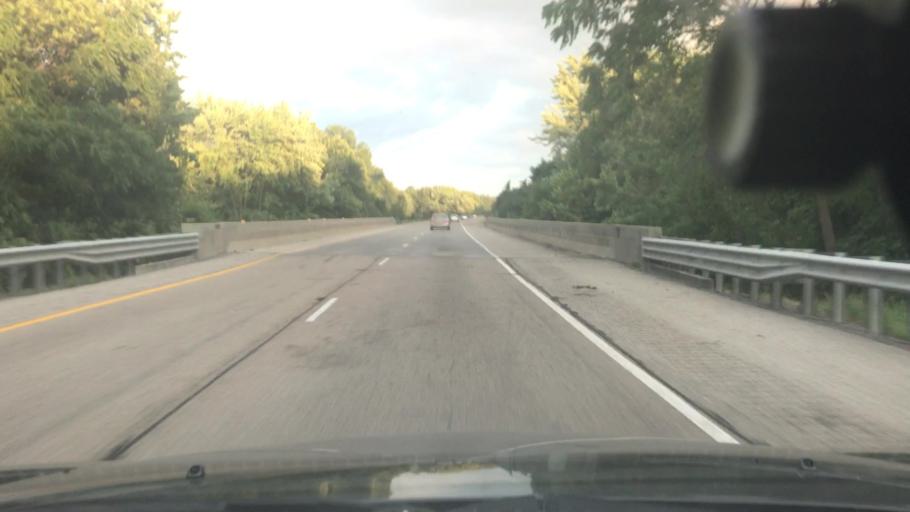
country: US
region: Illinois
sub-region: Washington County
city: Okawville
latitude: 38.4792
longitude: -89.5830
